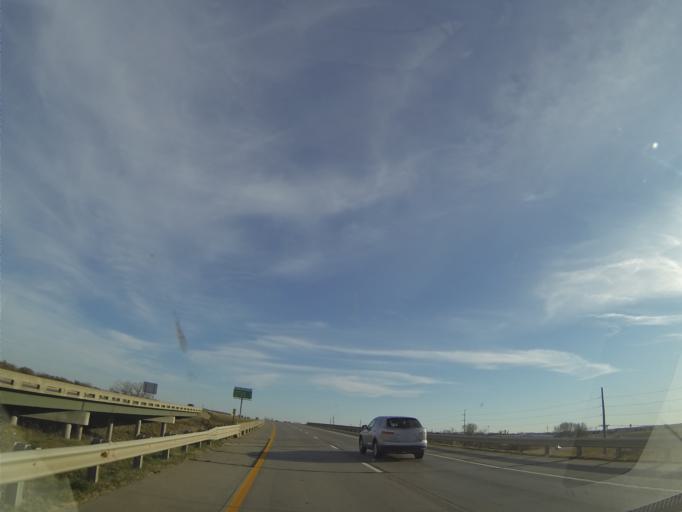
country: US
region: Kansas
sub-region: Saline County
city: Salina
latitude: 38.8124
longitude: -97.6331
